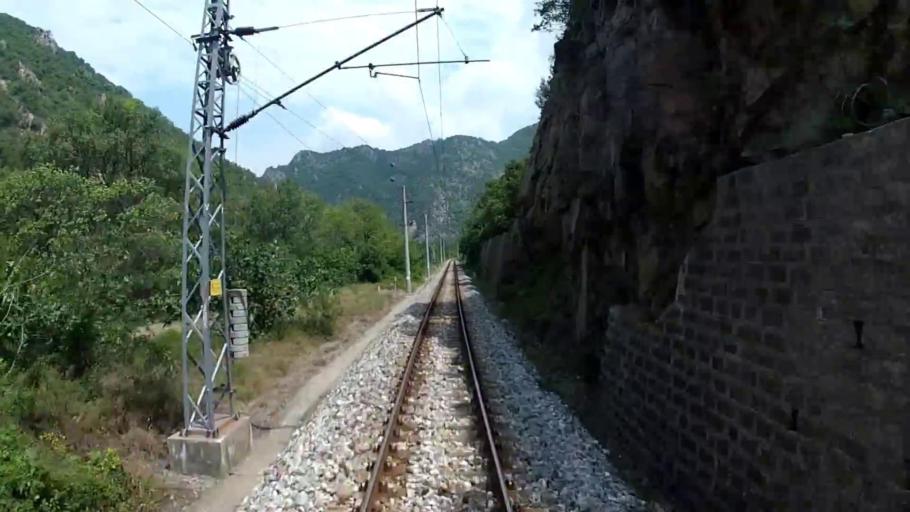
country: BG
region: Blagoevgrad
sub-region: Obshtina Kresna
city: Stara Kresna
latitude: 41.8053
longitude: 23.1637
